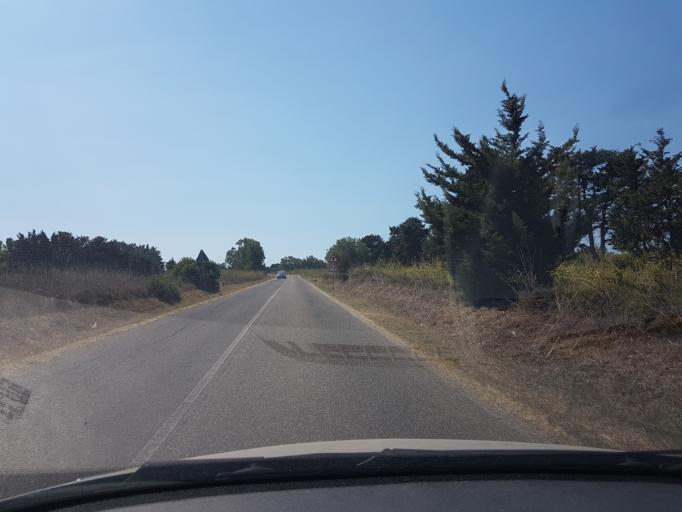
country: IT
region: Sardinia
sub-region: Provincia di Oristano
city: Riola Sardo
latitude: 39.9982
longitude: 8.4918
